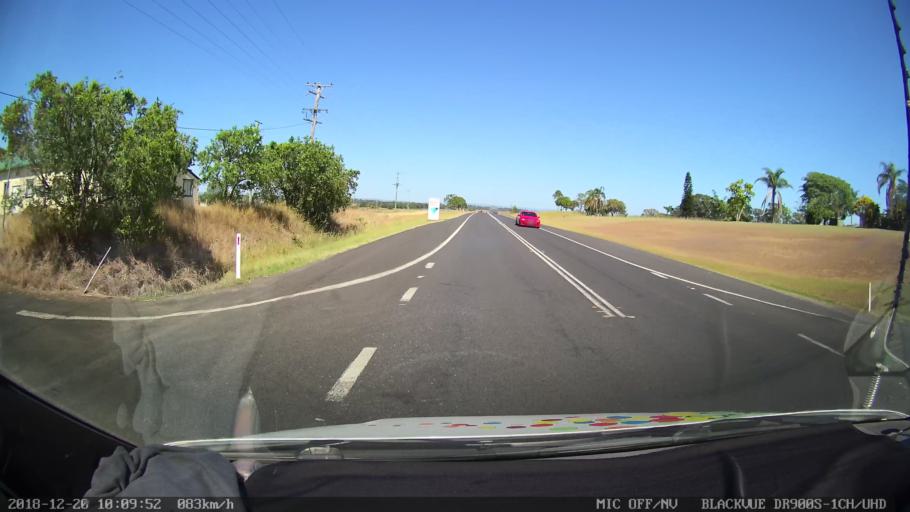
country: AU
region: New South Wales
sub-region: Lismore Municipality
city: Lismore
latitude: -28.8763
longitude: 153.1816
